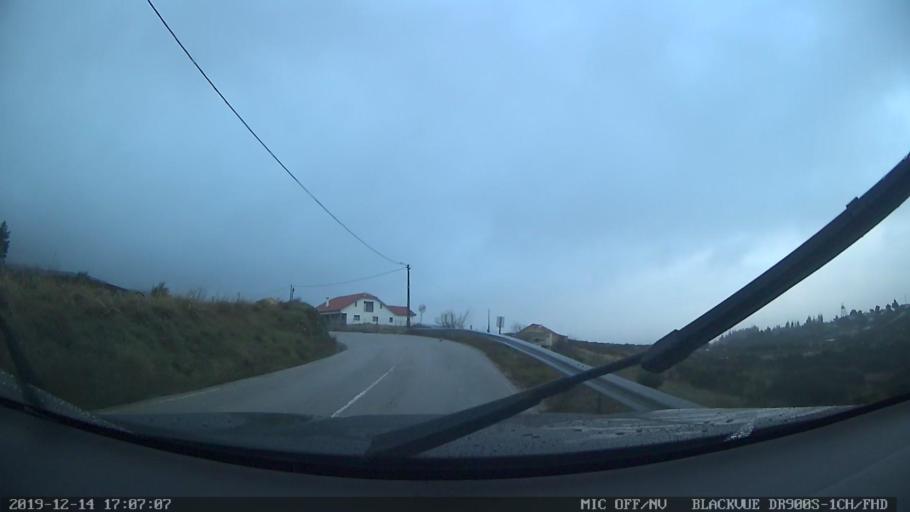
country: PT
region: Vila Real
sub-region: Vila Pouca de Aguiar
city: Vila Pouca de Aguiar
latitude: 41.4596
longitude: -7.5965
